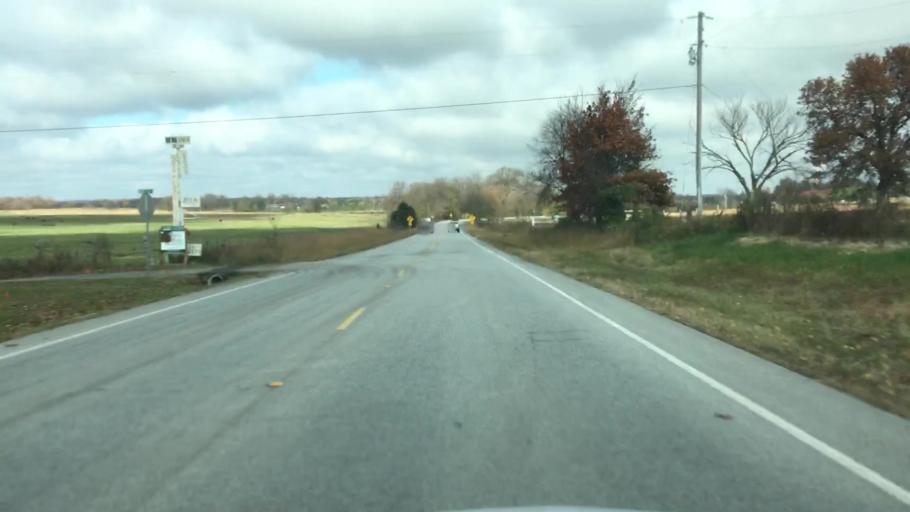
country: US
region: Arkansas
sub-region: Benton County
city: Centerton
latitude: 36.2831
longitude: -94.3501
